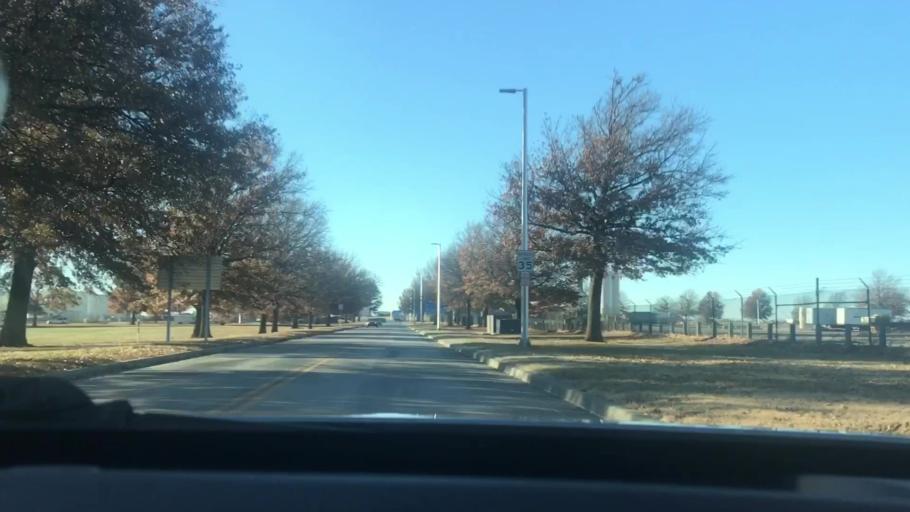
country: US
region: Missouri
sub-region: Platte County
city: Weatherby Lake
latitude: 39.3121
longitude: -94.7123
